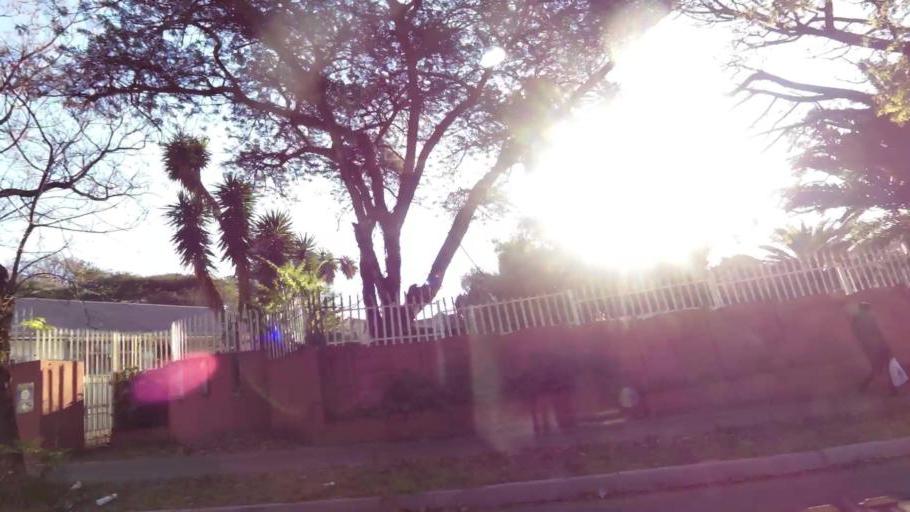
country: ZA
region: Gauteng
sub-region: City of Johannesburg Metropolitan Municipality
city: Johannesburg
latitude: -26.1866
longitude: 28.0054
